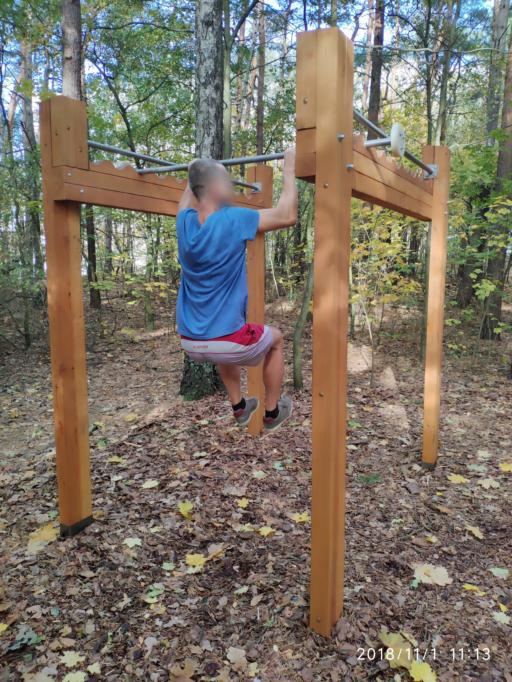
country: PL
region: Lubusz
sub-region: Zielona Gora
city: Zielona Gora
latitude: 51.9332
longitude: 15.5306
